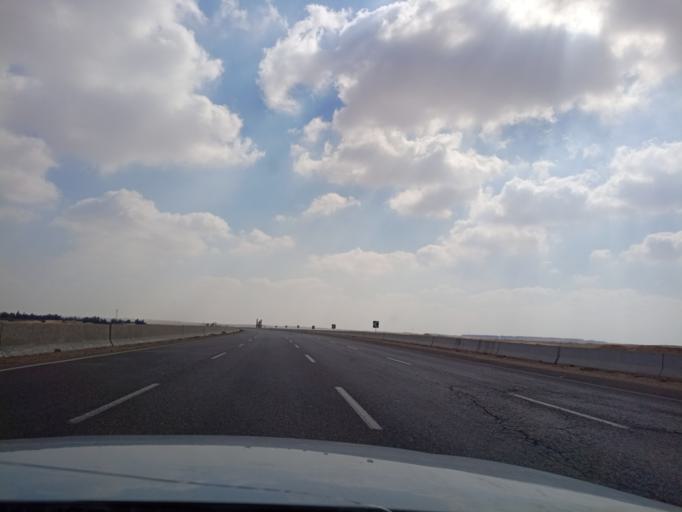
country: EG
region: Eastern Province
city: Bilbays
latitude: 30.3136
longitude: 31.5642
